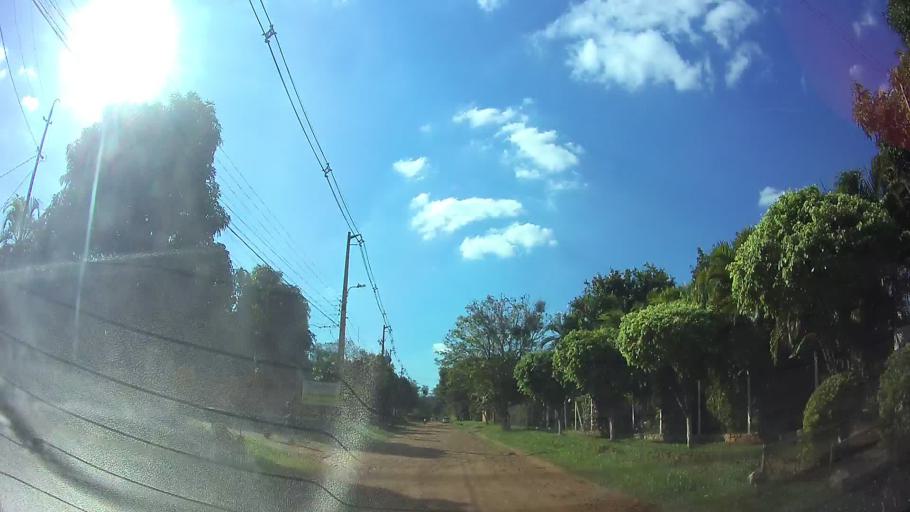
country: PY
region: Central
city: Limpio
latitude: -25.2537
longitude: -57.4749
